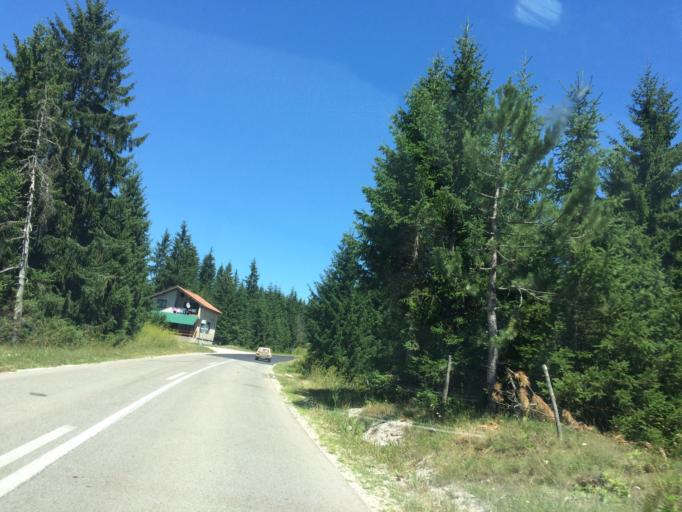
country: ME
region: Pljevlja
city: Pljevlja
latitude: 43.3435
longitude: 19.4953
